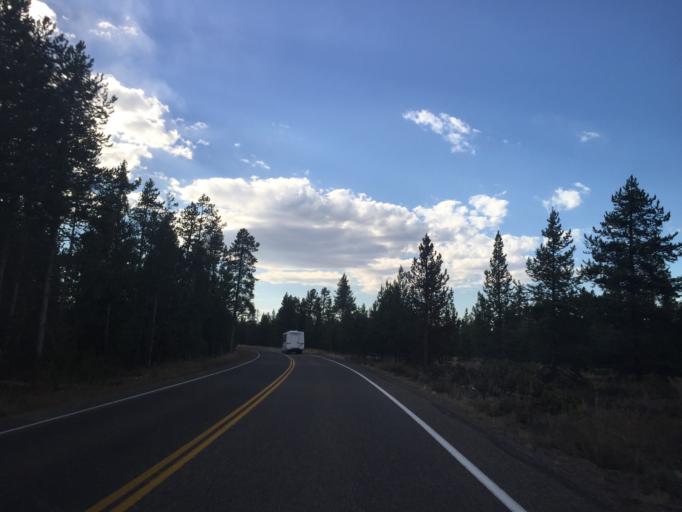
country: US
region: Montana
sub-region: Gallatin County
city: West Yellowstone
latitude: 44.6533
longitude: -111.0638
